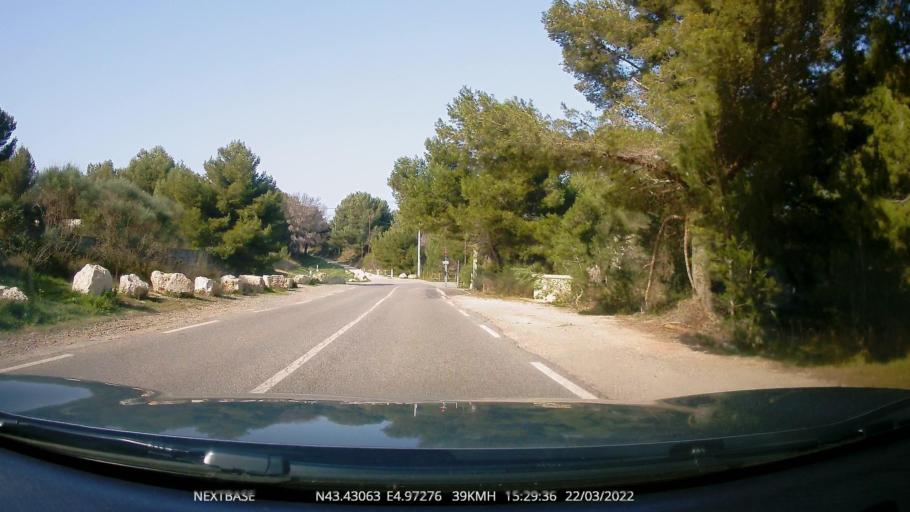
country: FR
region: Provence-Alpes-Cote d'Azur
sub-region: Departement des Bouches-du-Rhone
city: Port-de-Bouc
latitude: 43.4307
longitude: 4.9728
